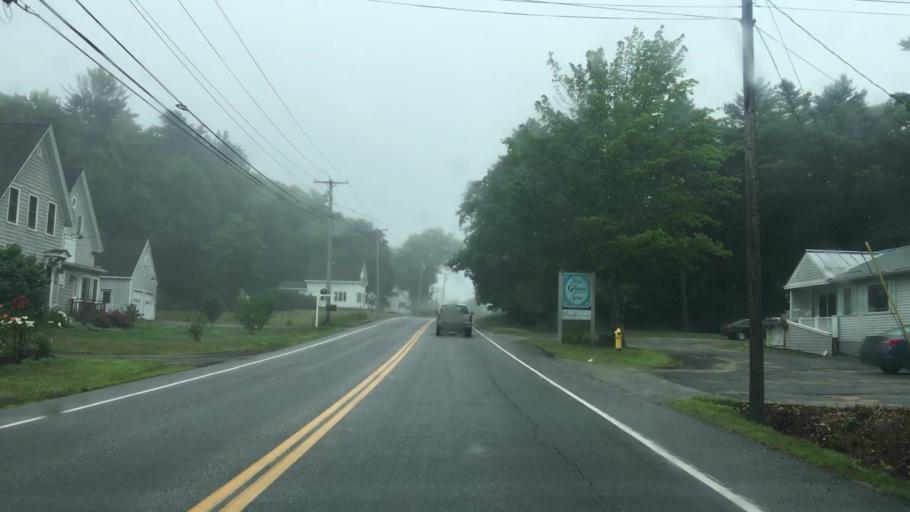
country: US
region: Maine
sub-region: Lincoln County
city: Boothbay
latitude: 43.8821
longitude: -69.6319
